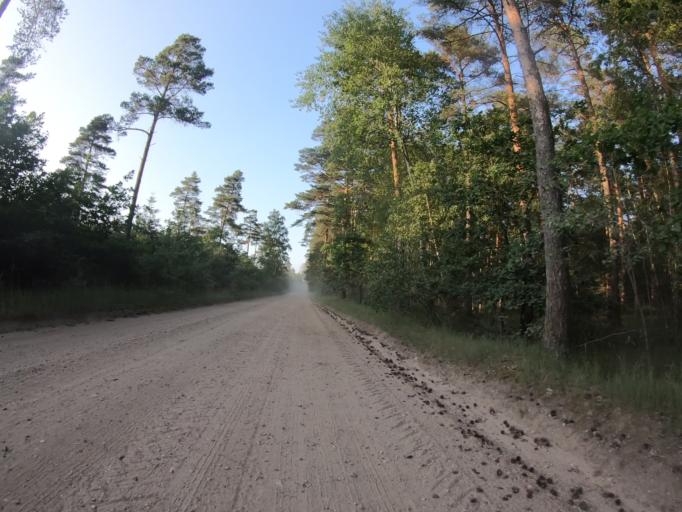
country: DE
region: Lower Saxony
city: Wagenhoff
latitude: 52.5448
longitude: 10.5014
